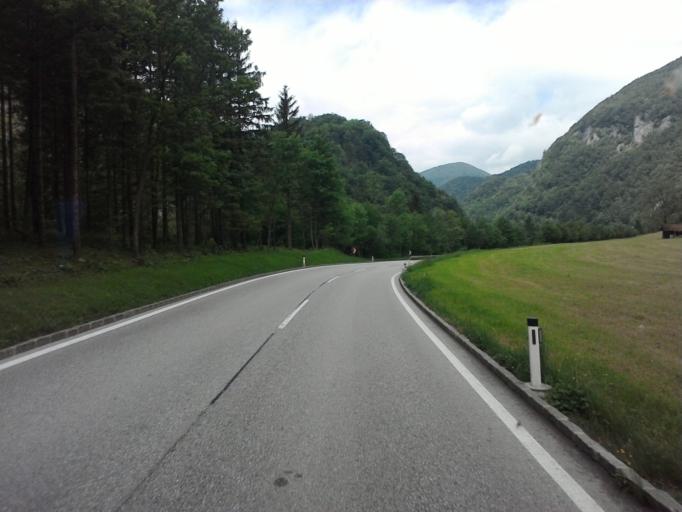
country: AT
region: Upper Austria
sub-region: Politischer Bezirk Steyr-Land
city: Weyer
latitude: 47.8638
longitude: 14.6103
